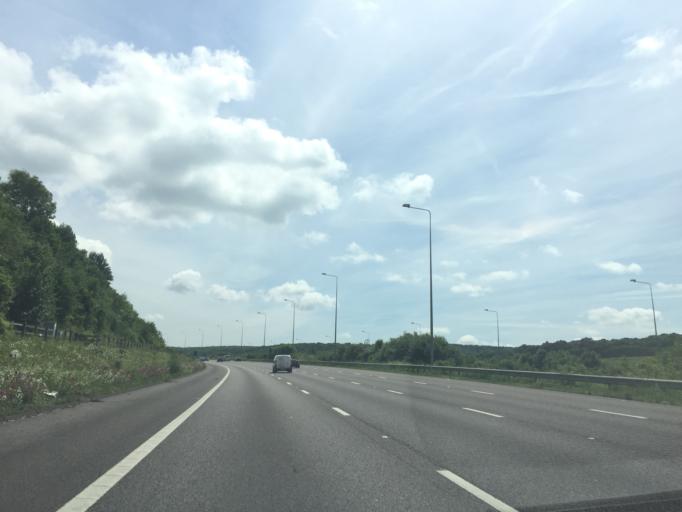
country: GB
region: England
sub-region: Medway
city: Rochester
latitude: 51.3634
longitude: 0.4901
